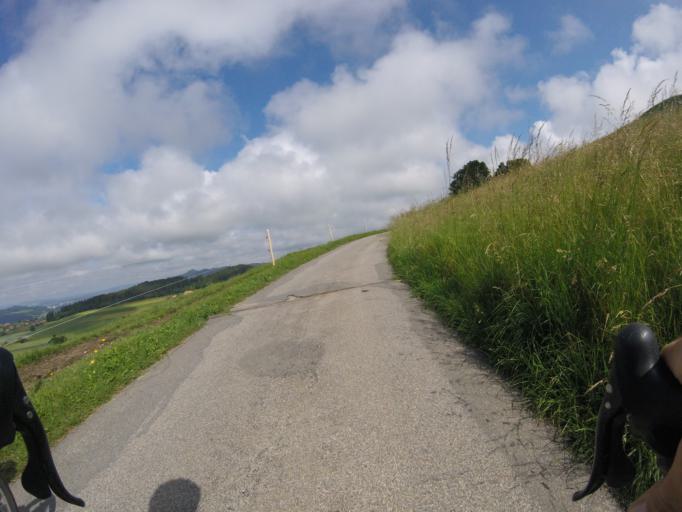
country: CH
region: Bern
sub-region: Bern-Mittelland District
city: Walkringen
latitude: 46.9532
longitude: 7.5999
